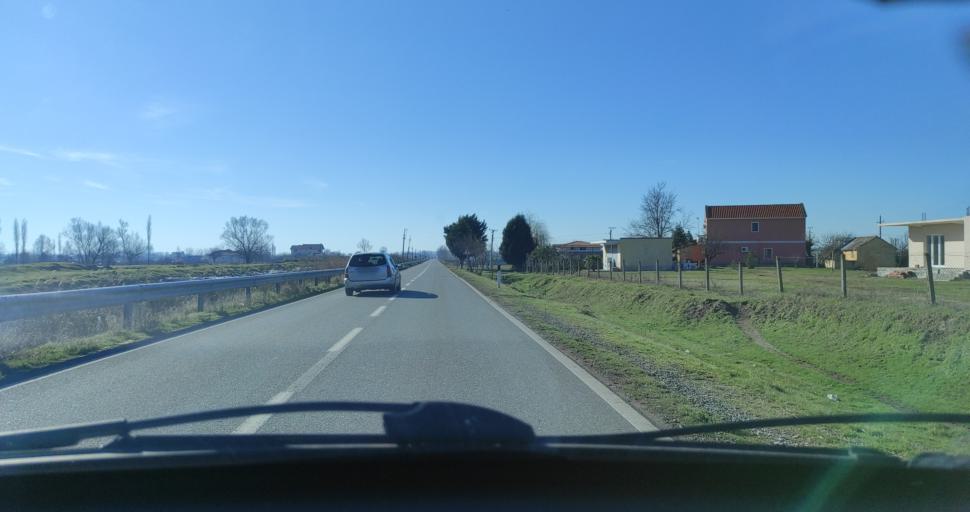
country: AL
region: Shkoder
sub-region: Rrethi i Shkodres
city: Velipoje
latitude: 41.8915
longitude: 19.4033
